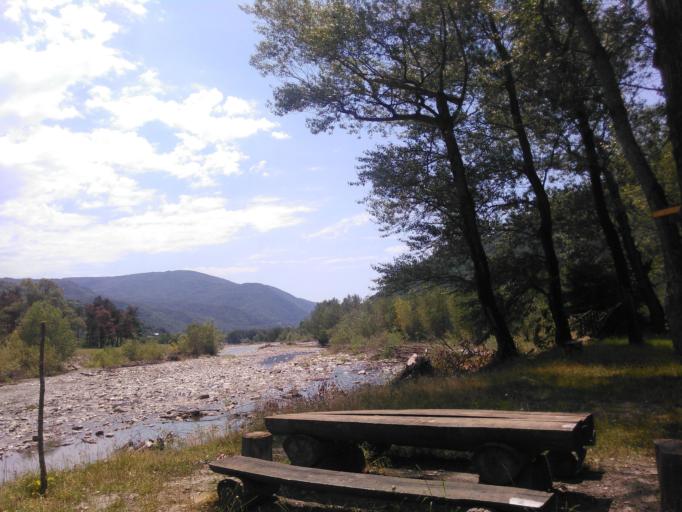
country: GE
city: Zhinvali
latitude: 42.2197
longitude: 44.8314
